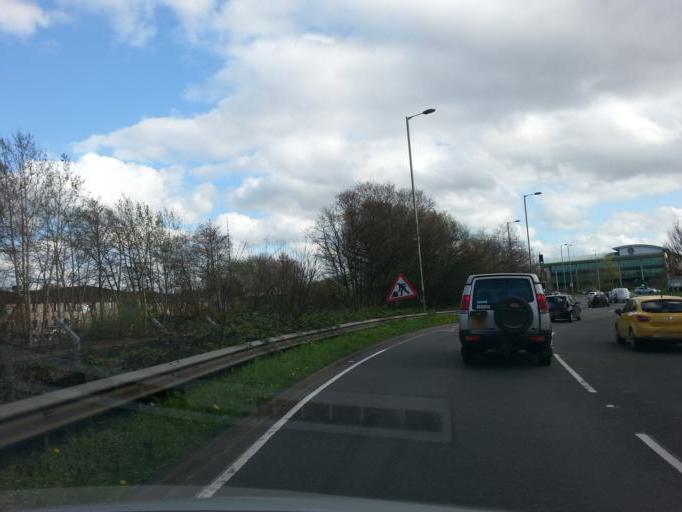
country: GB
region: England
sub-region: Surrey
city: Frimley
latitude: 51.3159
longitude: -0.7544
